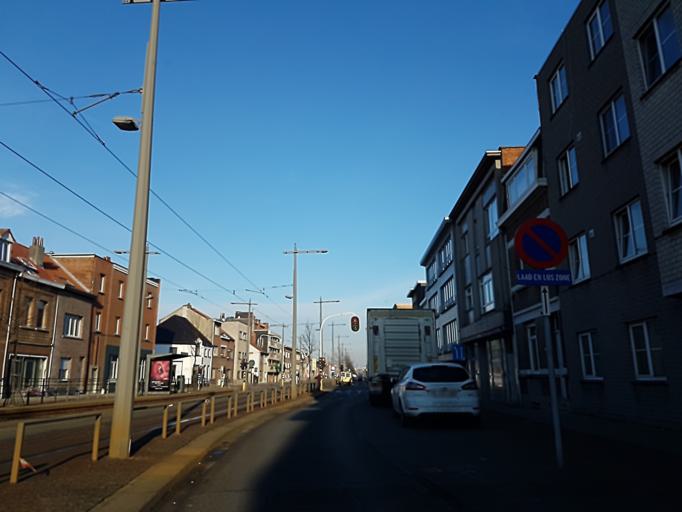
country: BE
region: Flanders
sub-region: Provincie Antwerpen
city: Hoboken
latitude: 51.1772
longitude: 4.3684
